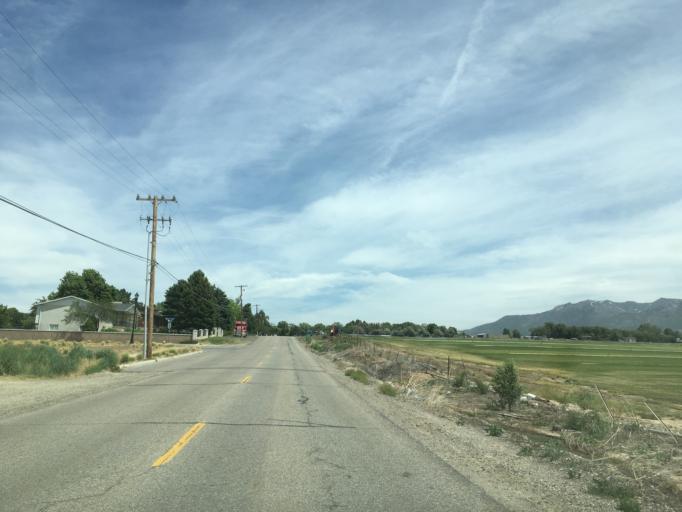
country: US
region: Utah
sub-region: Davis County
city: Hill Air Force Bace
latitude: 41.0906
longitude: -111.9596
